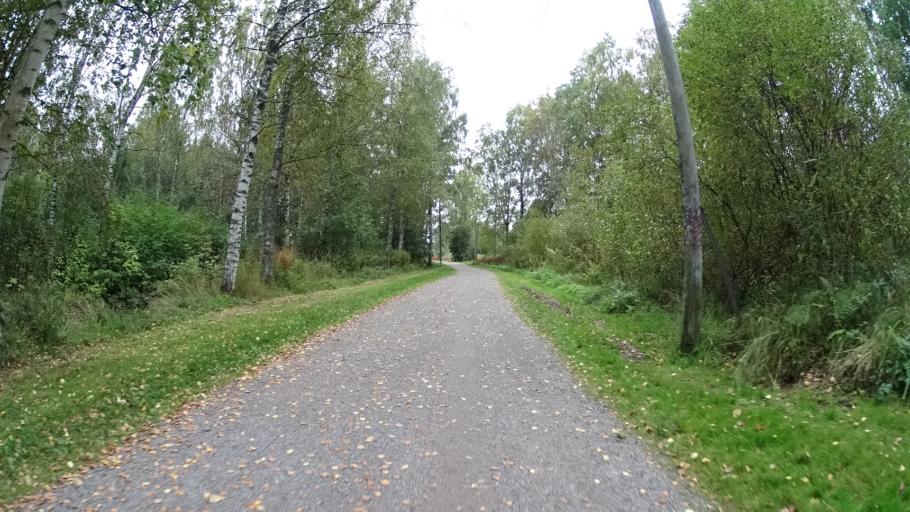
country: FI
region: Uusimaa
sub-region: Helsinki
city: Kauniainen
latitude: 60.2086
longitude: 24.7164
